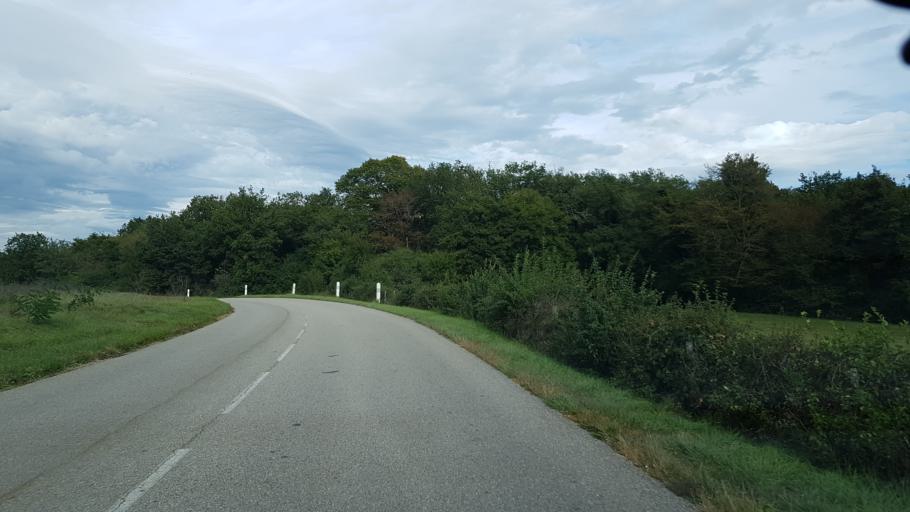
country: FR
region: Rhone-Alpes
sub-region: Departement de l'Ain
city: Villereversure
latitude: 46.1682
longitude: 5.3631
